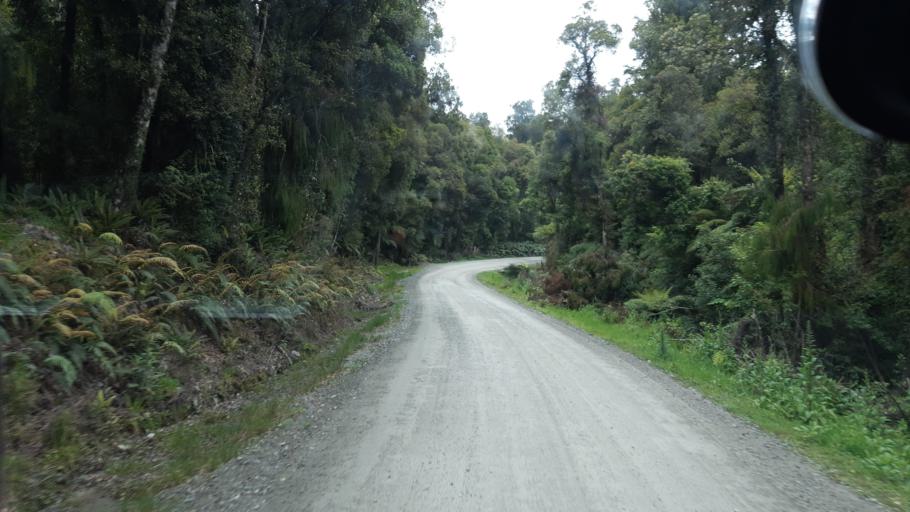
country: NZ
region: West Coast
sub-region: Grey District
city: Greymouth
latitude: -42.6450
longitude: 171.3479
